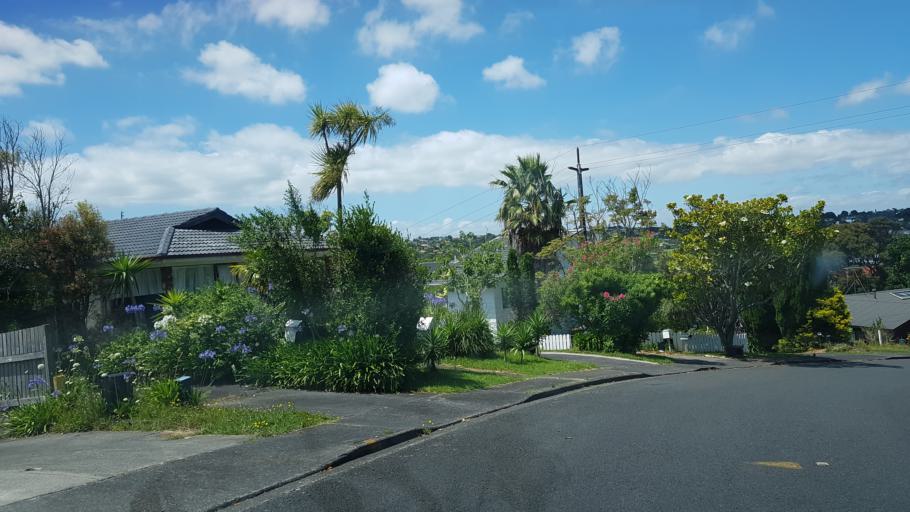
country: NZ
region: Auckland
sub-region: Auckland
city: North Shore
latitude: -36.7774
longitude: 174.7128
